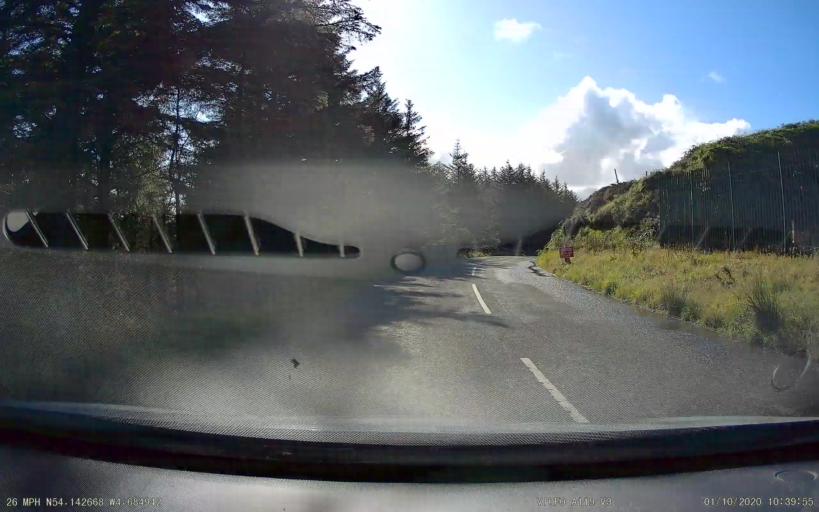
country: IM
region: Castletown
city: Castletown
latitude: 54.1427
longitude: -4.6840
